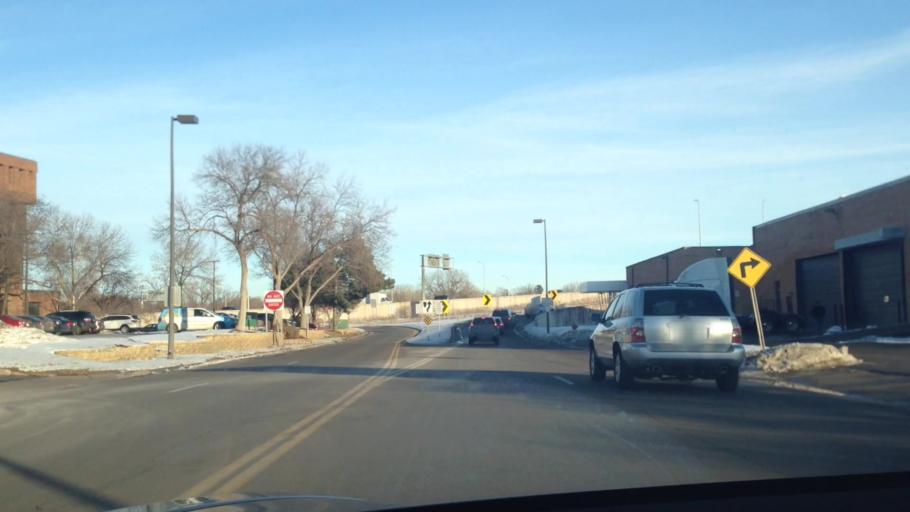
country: US
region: Minnesota
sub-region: Hennepin County
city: Saint Louis Park
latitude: 44.9637
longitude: -93.3462
